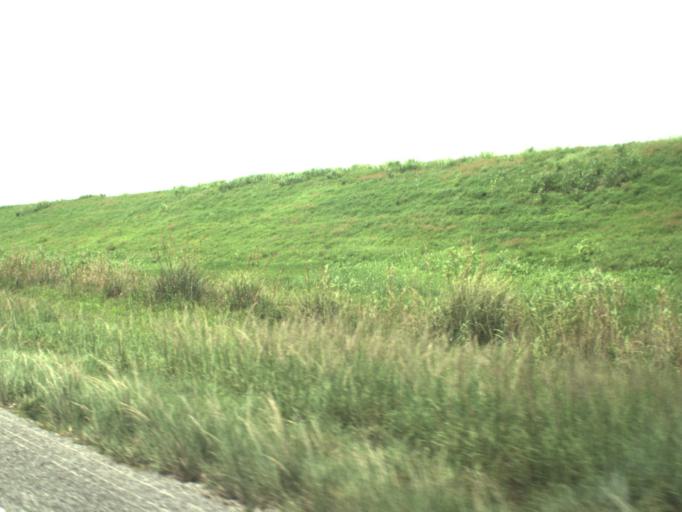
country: US
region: Florida
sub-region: Hendry County
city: Clewiston
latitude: 26.7416
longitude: -80.8812
